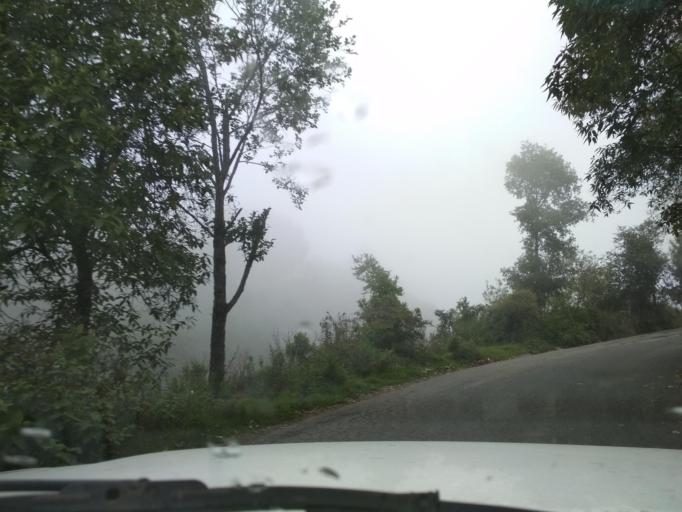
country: MX
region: Veracruz
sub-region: Mariano Escobedo
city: Loma Grande
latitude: 18.9341
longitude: -97.2212
